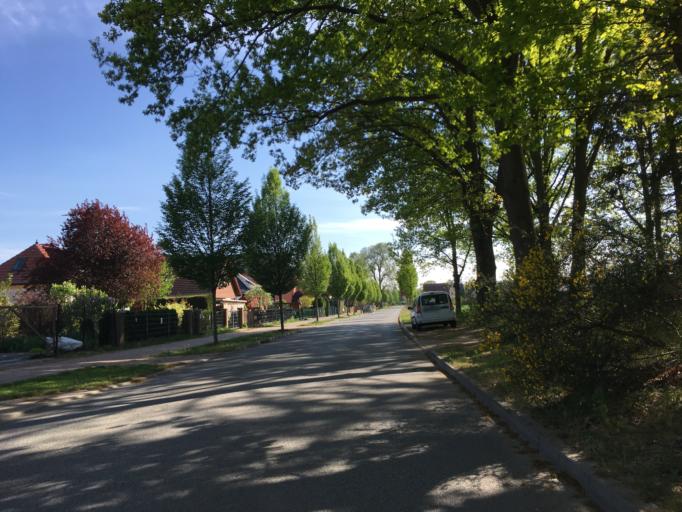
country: DE
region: Berlin
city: Buch
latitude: 52.6595
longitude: 13.5210
